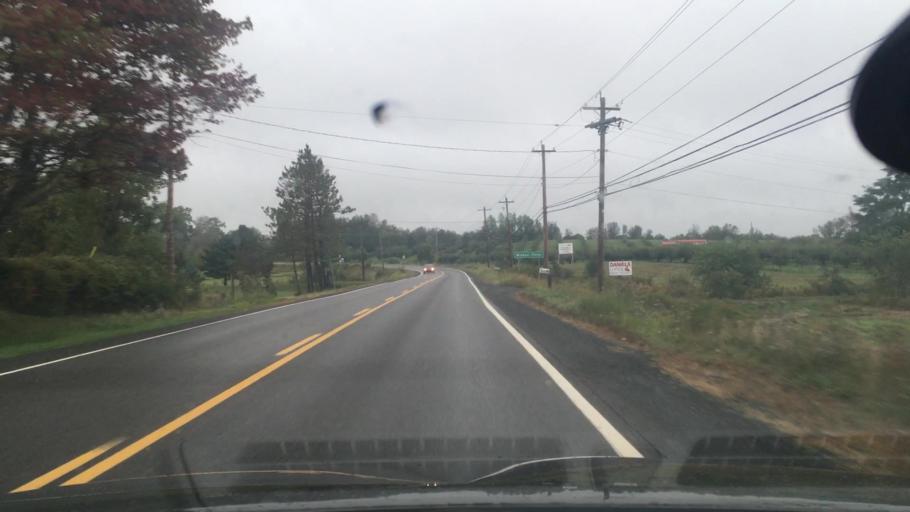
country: CA
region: Nova Scotia
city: Windsor
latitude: 44.9507
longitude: -64.1704
